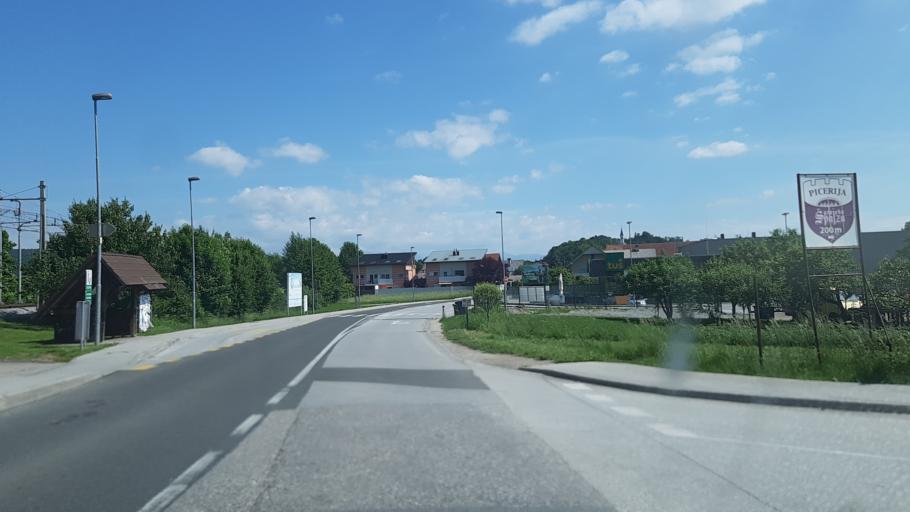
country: SI
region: Brezovica
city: Notranje Gorice
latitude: 45.9957
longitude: 14.4064
